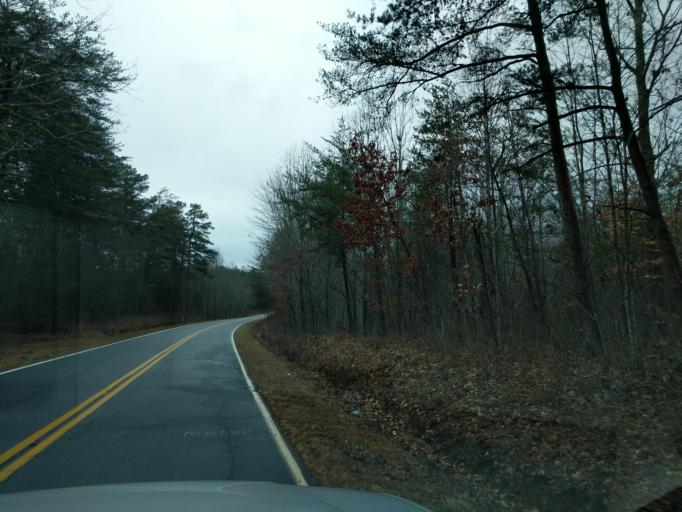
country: US
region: South Carolina
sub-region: Oconee County
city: Walhalla
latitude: 34.7970
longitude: -83.1620
